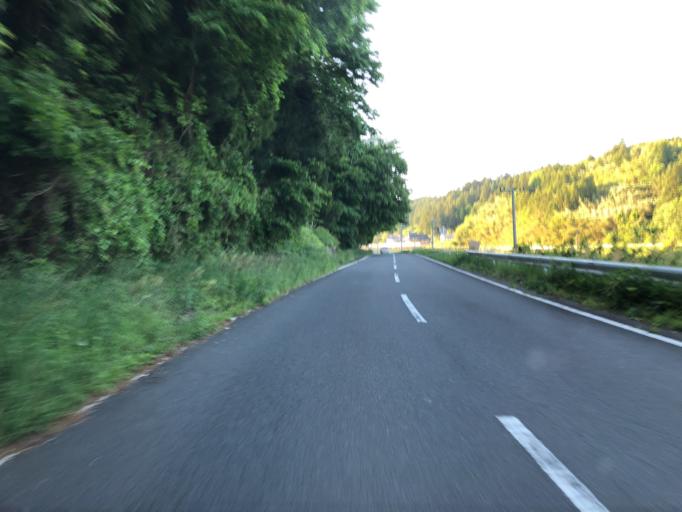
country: JP
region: Fukushima
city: Ishikawa
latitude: 36.9936
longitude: 140.4380
